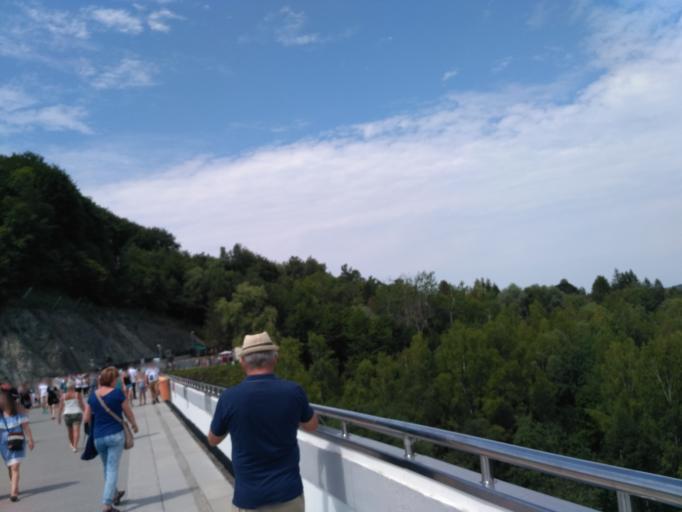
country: PL
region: Subcarpathian Voivodeship
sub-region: Powiat leski
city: Polanczyk
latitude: 49.3966
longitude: 22.4516
